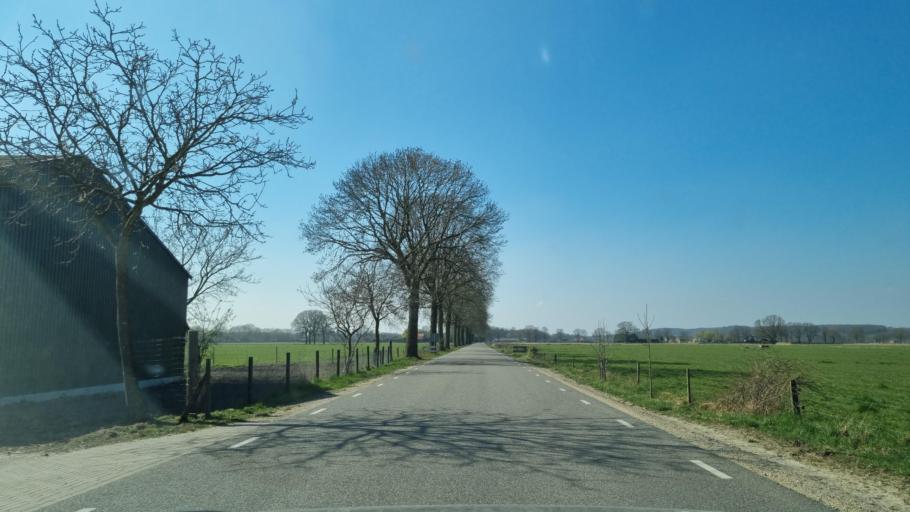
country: NL
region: Limburg
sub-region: Gemeente Gennep
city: Gennep
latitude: 51.7264
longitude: 5.9790
